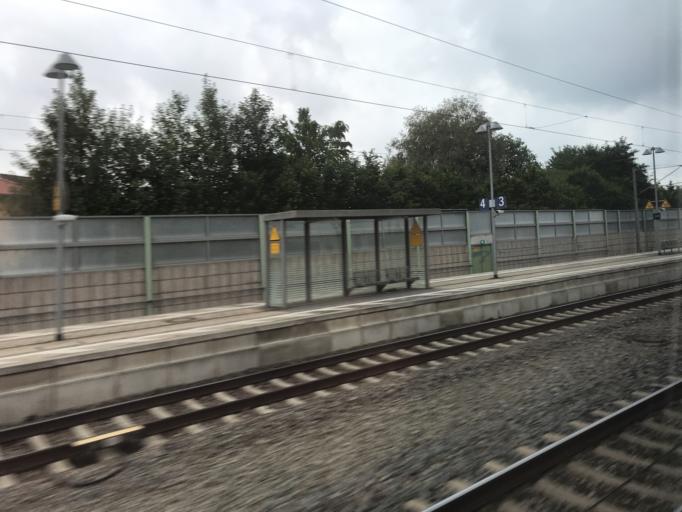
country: DE
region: Bavaria
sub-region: Upper Bavaria
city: Althegnenberg
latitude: 48.2366
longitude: 11.0632
